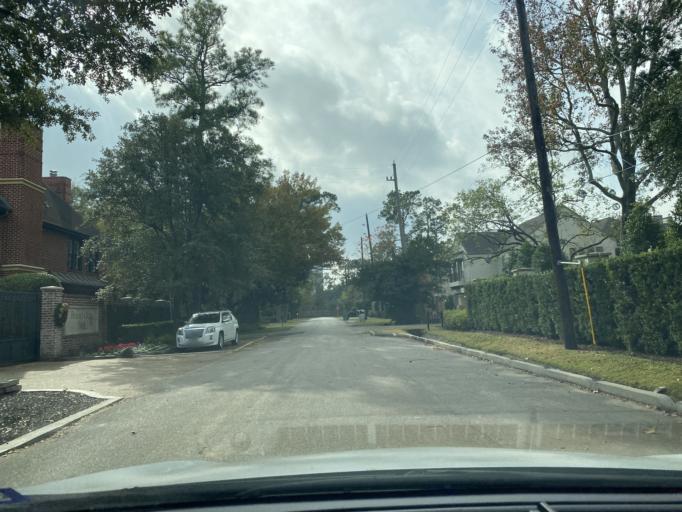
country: US
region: Texas
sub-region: Harris County
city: Hunters Creek Village
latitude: 29.7653
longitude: -95.4726
